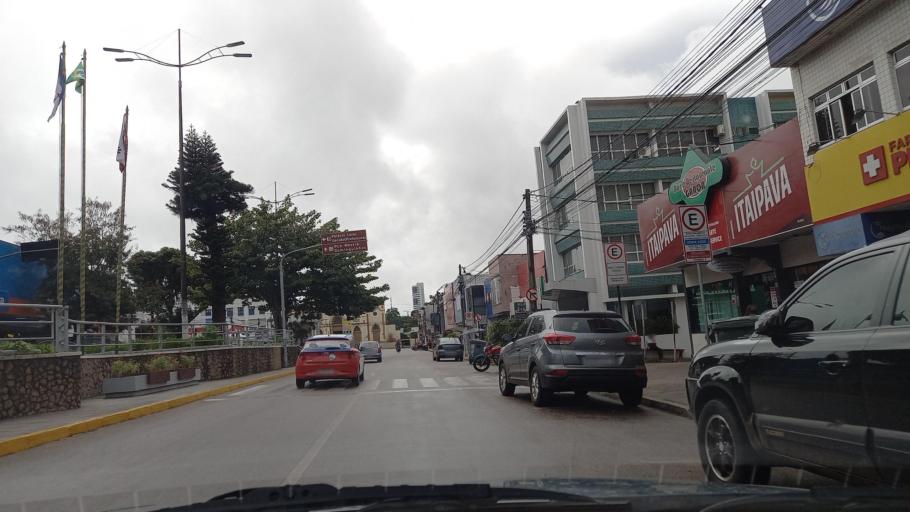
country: BR
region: Pernambuco
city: Garanhuns
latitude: -8.8909
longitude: -36.4932
